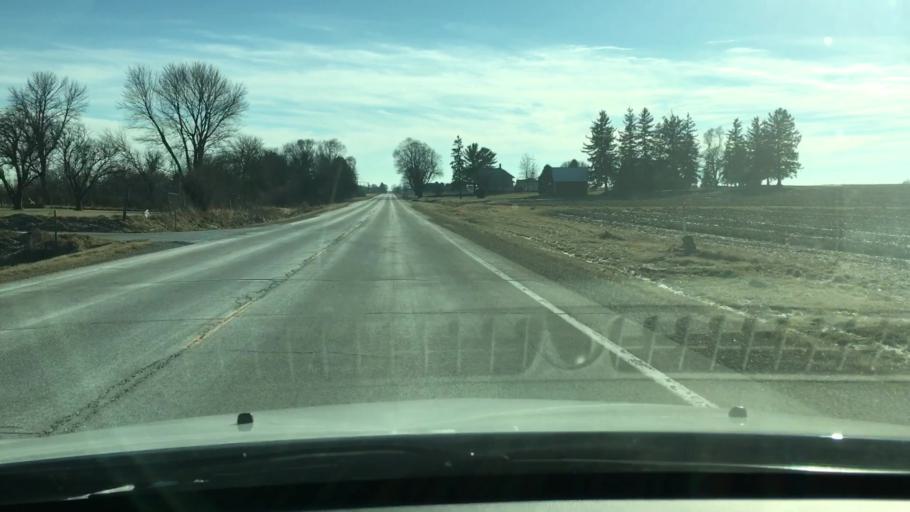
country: US
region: Illinois
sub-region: LaSalle County
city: Mendota
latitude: 41.5845
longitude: -89.1283
